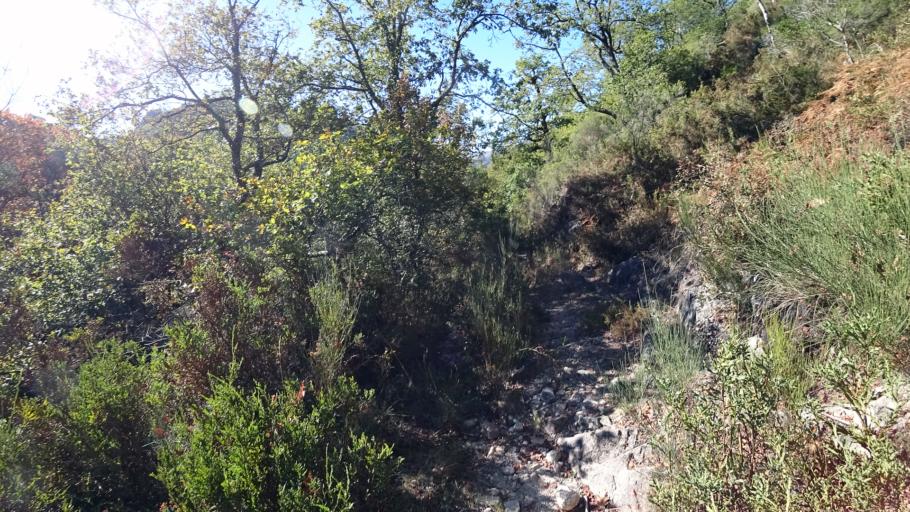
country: ES
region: Galicia
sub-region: Provincia de Ourense
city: Lobios
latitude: 41.7949
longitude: -8.1368
